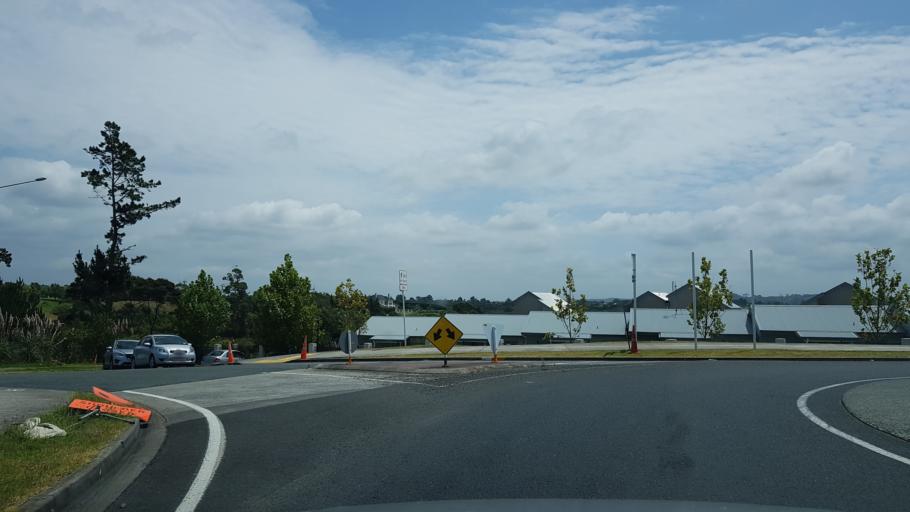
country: NZ
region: Auckland
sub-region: Auckland
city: Rosebank
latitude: -36.7909
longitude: 174.6544
